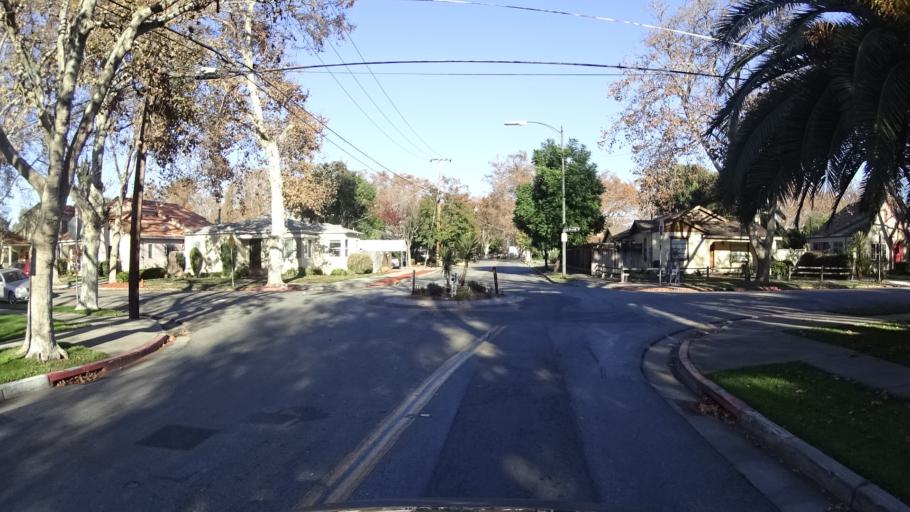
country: US
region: California
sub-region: Santa Clara County
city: San Jose
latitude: 37.3575
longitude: -121.9054
